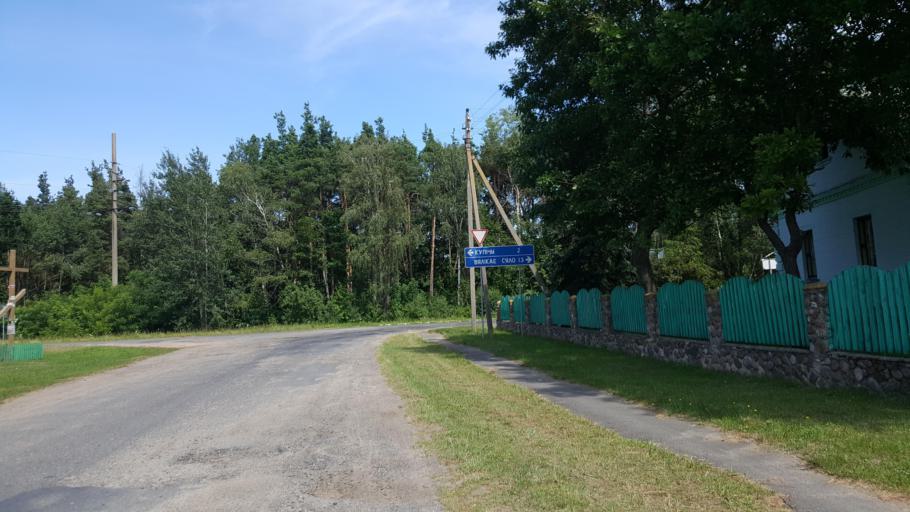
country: BY
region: Brest
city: Pruzhany
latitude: 52.5675
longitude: 24.2090
